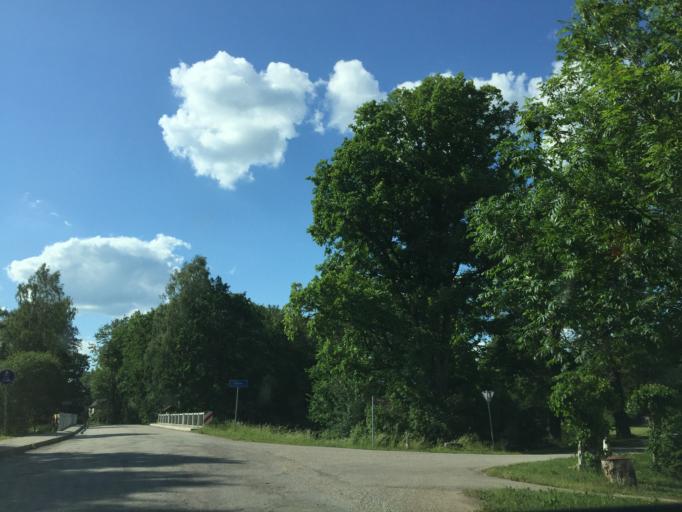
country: LV
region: Jaunpils
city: Jaunpils
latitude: 56.8737
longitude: 22.9996
